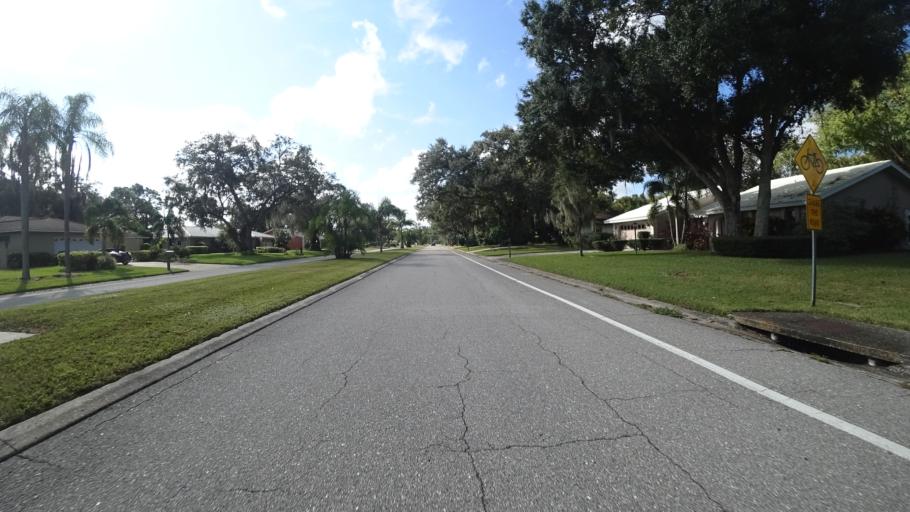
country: US
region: Florida
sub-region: Sarasota County
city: Desoto Lakes
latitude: 27.4036
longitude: -82.5008
